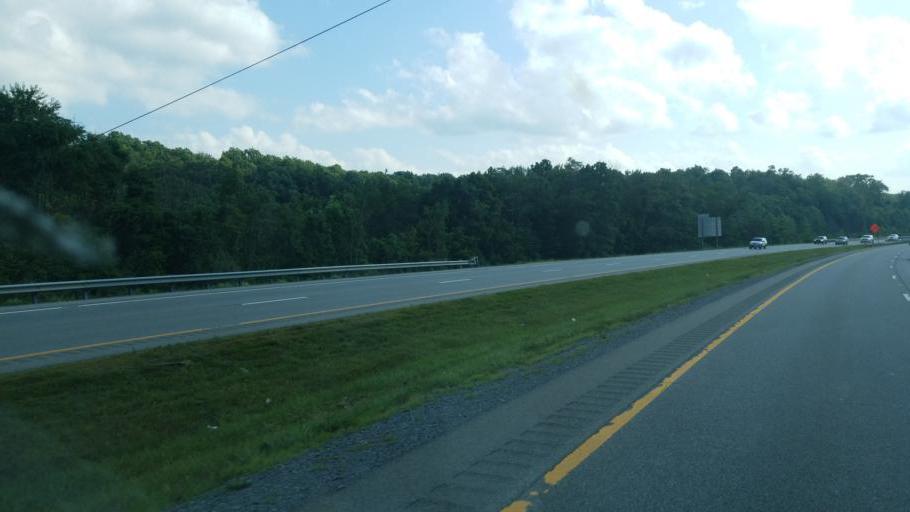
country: US
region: West Virginia
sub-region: Monongalia County
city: Brookhaven
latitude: 39.6291
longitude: -79.9019
